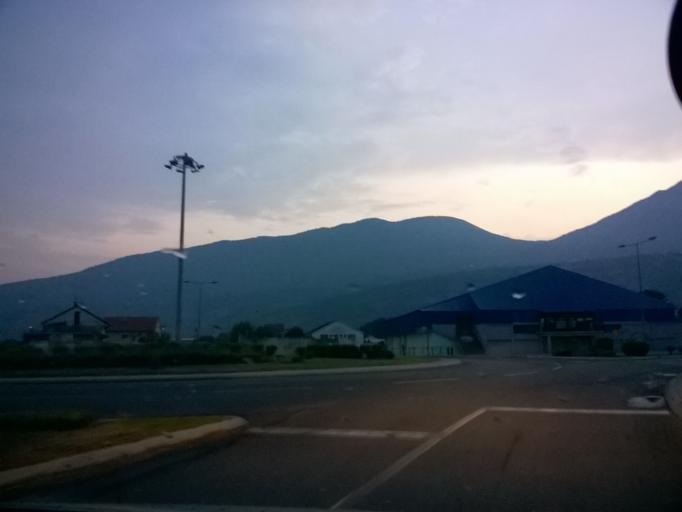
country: ME
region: Danilovgrad
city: Danilovgrad
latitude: 42.5471
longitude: 19.1003
